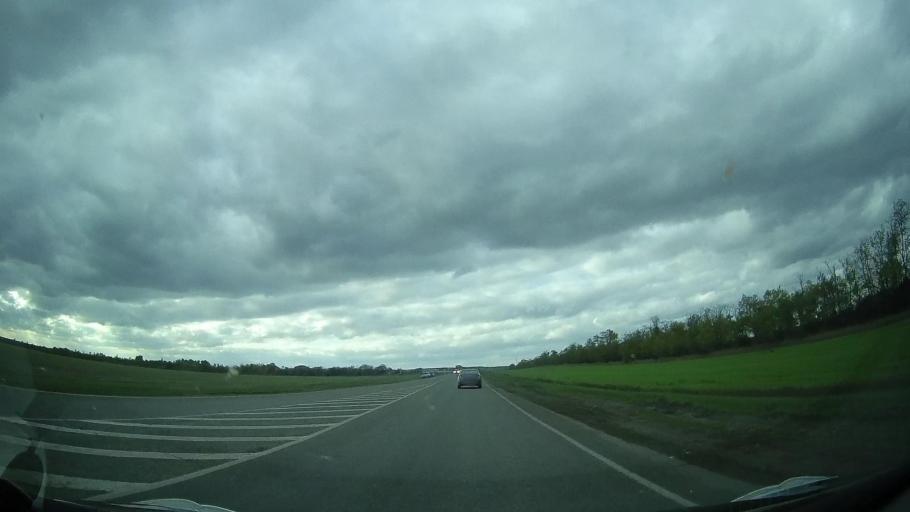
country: RU
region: Rostov
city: Kagal'nitskaya
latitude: 46.8703
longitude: 40.1684
